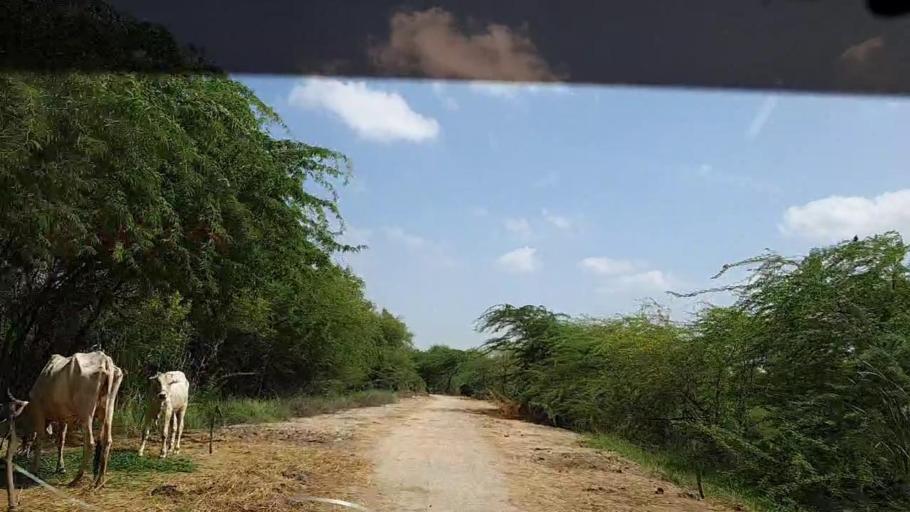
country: PK
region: Sindh
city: Badin
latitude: 24.5924
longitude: 68.7999
